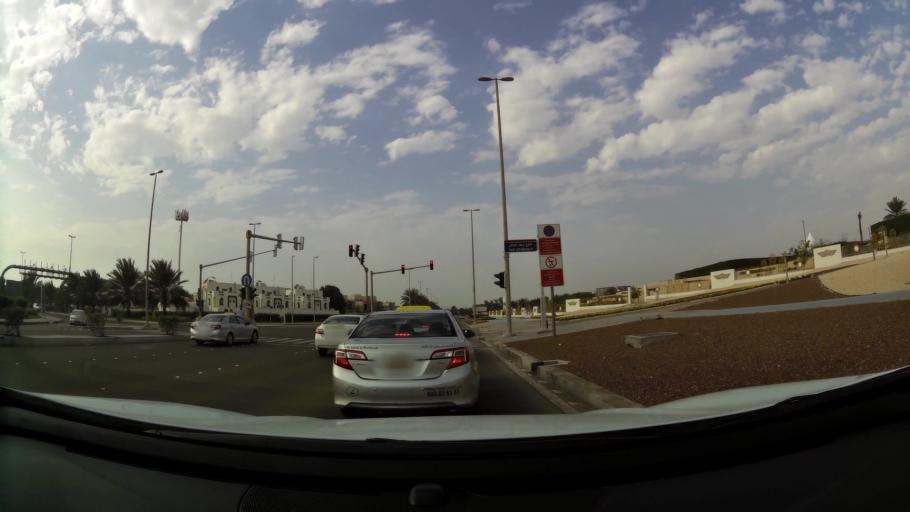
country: AE
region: Abu Dhabi
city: Abu Dhabi
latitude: 24.4135
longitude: 54.4725
